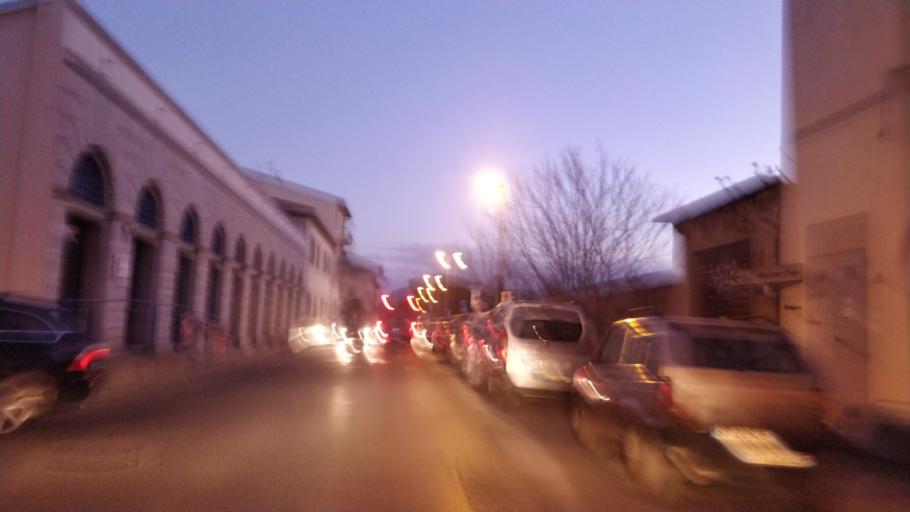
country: IT
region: Tuscany
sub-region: Provincia di Livorno
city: Cecina
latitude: 43.3126
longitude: 10.5137
